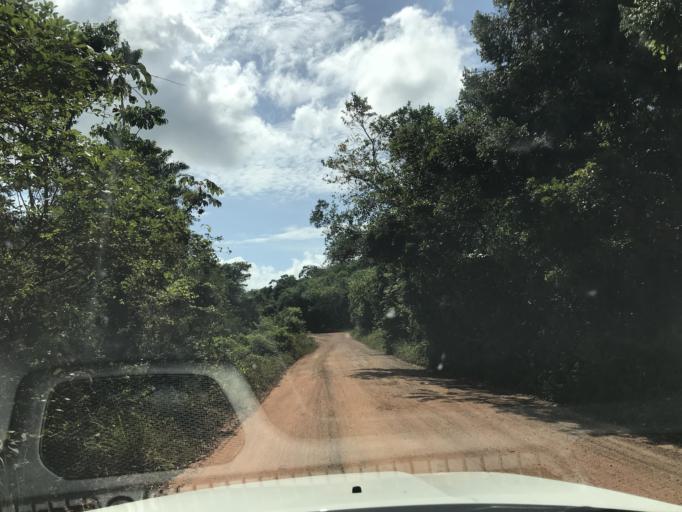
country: BR
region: Bahia
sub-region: Entre Rios
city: Entre Rios
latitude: -12.1666
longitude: -38.0714
